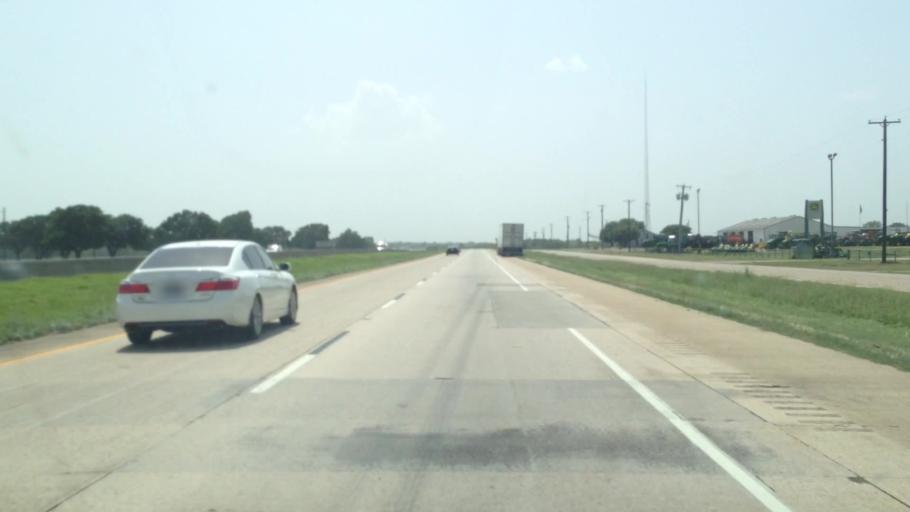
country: US
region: Texas
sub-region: Hopkins County
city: Sulphur Springs
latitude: 33.1209
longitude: -95.7002
